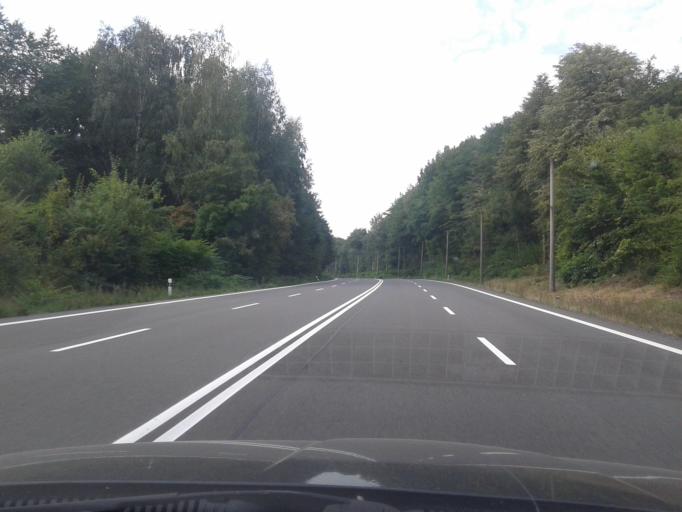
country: CZ
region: Moravskoslezsky
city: Orlova
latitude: 49.8306
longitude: 18.4355
